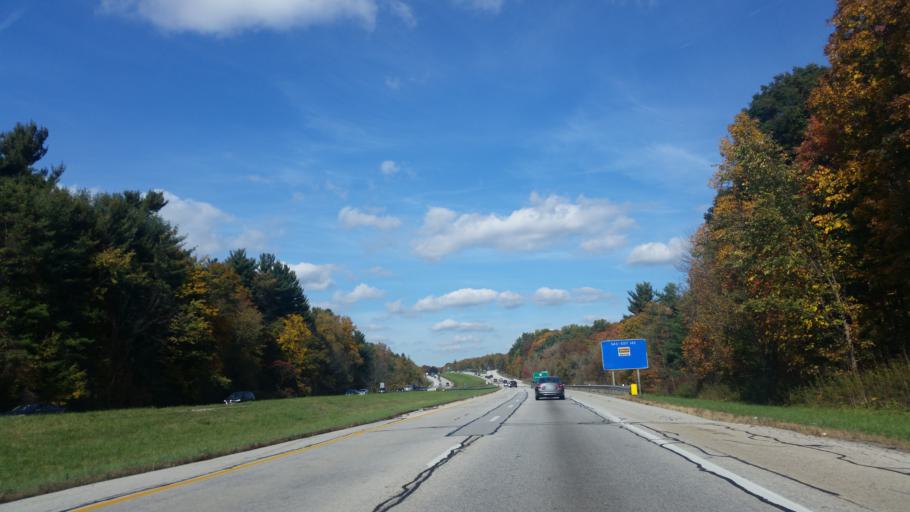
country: US
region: Ohio
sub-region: Summit County
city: Richfield
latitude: 41.2506
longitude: -81.6295
